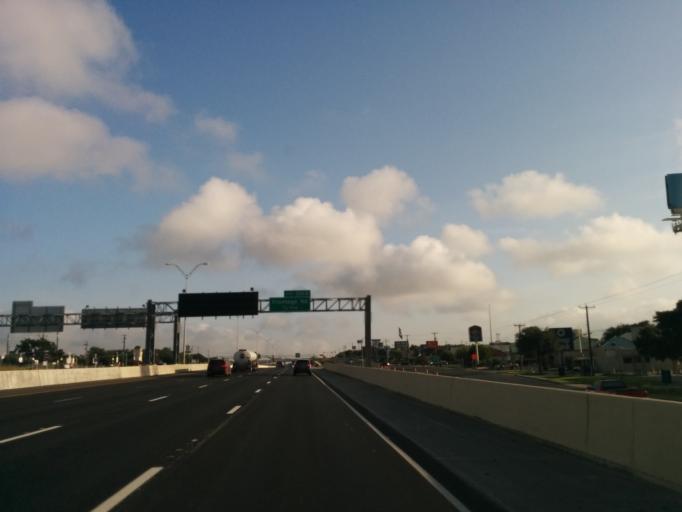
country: US
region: Texas
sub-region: Bexar County
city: Shavano Park
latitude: 29.5702
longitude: -98.5930
